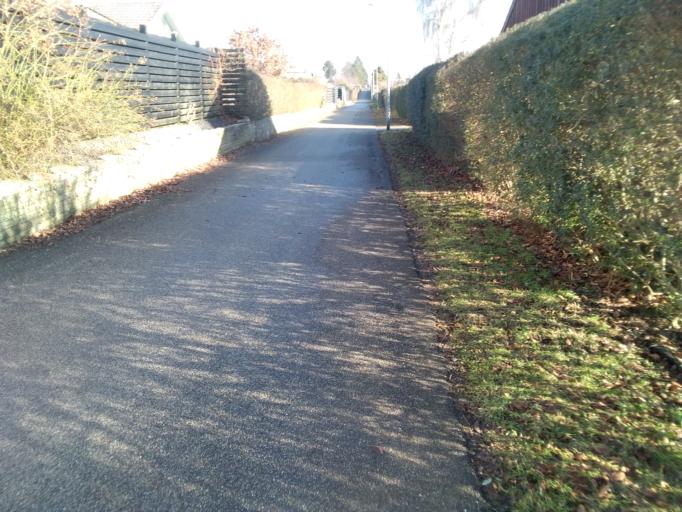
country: DK
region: Capital Region
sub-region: Egedal Kommune
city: Smorumnedre
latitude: 55.7433
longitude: 12.2985
